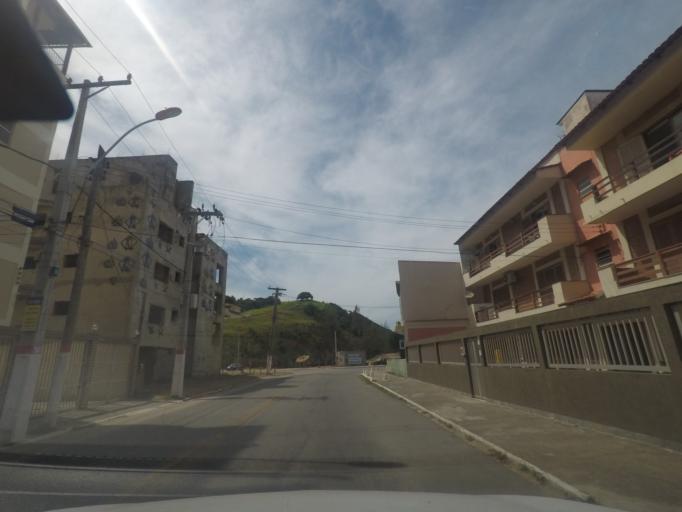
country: BR
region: Rio de Janeiro
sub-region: Marica
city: Marica
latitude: -22.9567
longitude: -42.6949
